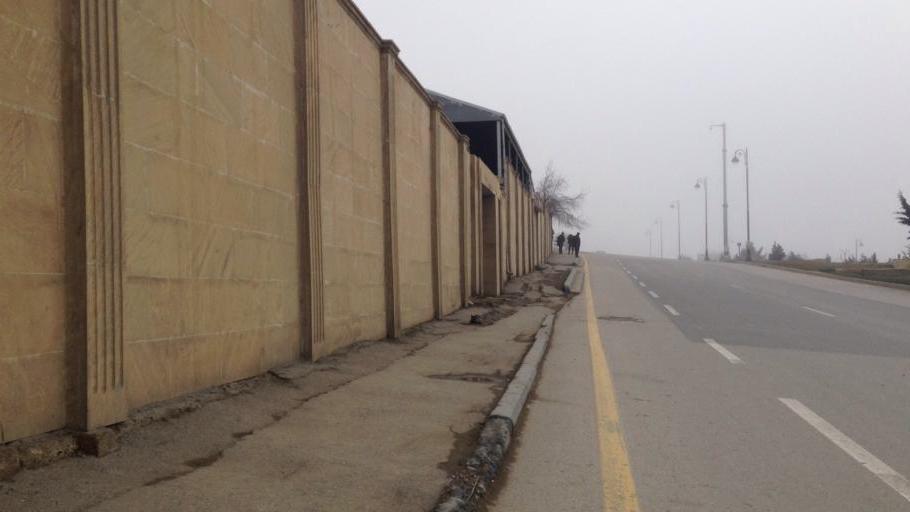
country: AZ
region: Baki
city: Qaracuxur
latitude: 40.3507
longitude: 49.9600
